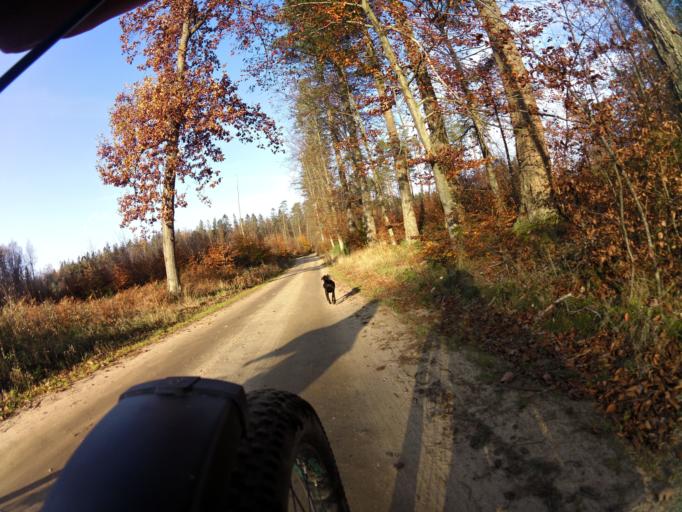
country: PL
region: Pomeranian Voivodeship
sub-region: Powiat pucki
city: Krokowa
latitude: 54.7261
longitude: 18.2159
